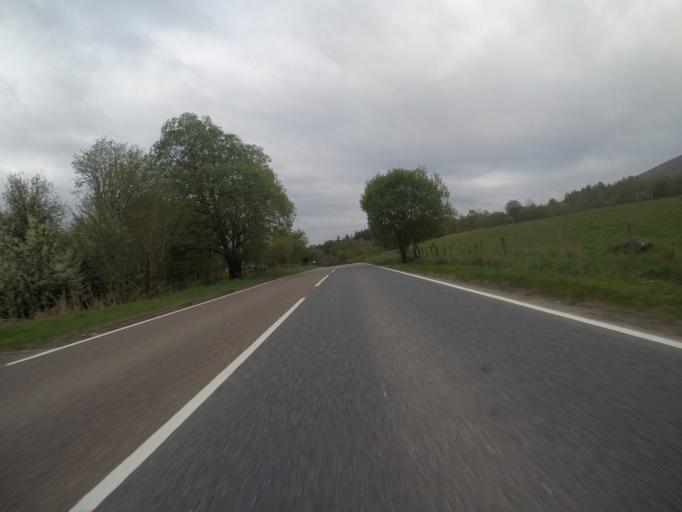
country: GB
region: Scotland
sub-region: Highland
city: Spean Bridge
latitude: 56.8908
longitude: -4.8711
